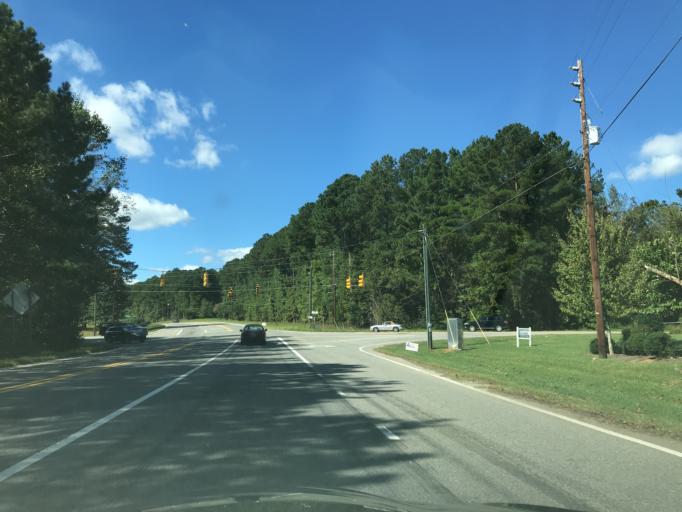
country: US
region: North Carolina
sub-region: Granville County
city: Creedmoor
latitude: 35.9890
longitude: -78.6949
